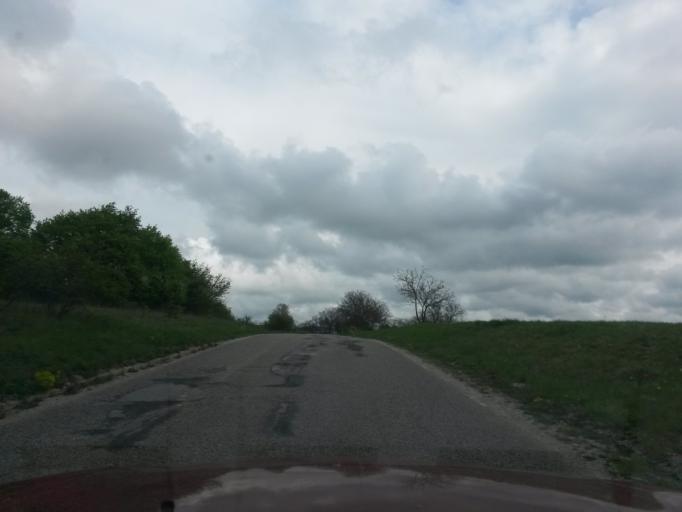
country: SK
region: Kosicky
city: Roznava
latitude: 48.5582
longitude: 20.5013
